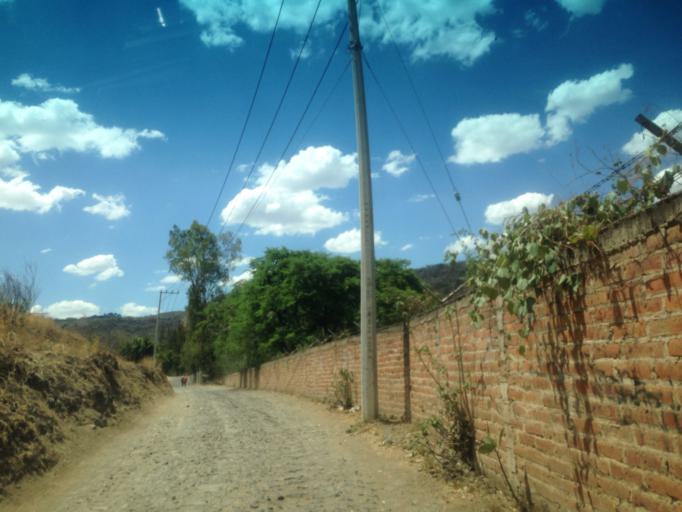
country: MX
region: Jalisco
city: Atotonilco el Alto
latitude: 20.5610
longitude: -102.5119
